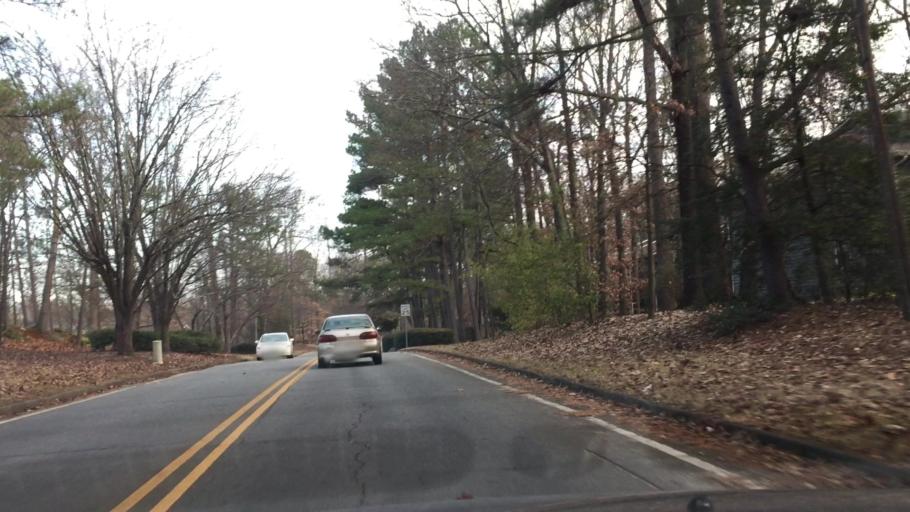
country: US
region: Georgia
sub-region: DeKalb County
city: Dunwoody
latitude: 33.9727
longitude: -84.3629
